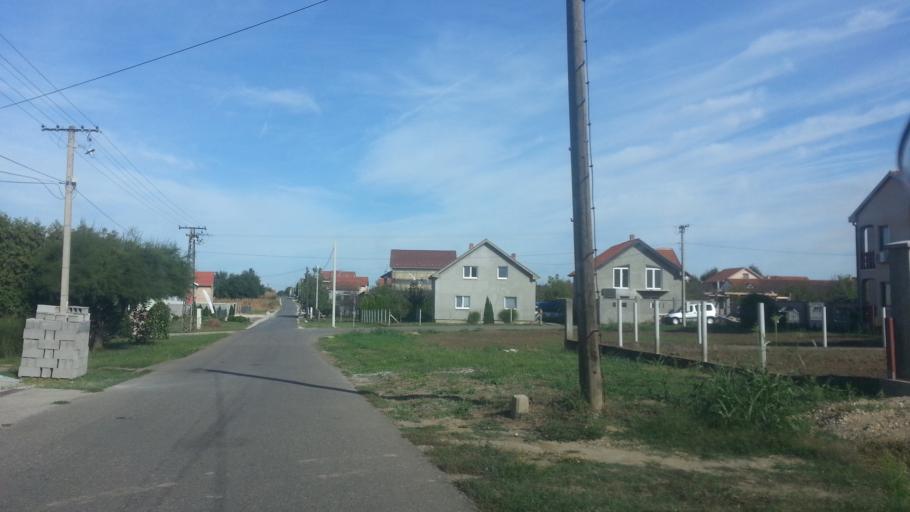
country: RS
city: Novi Banovci
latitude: 44.9705
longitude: 20.2756
